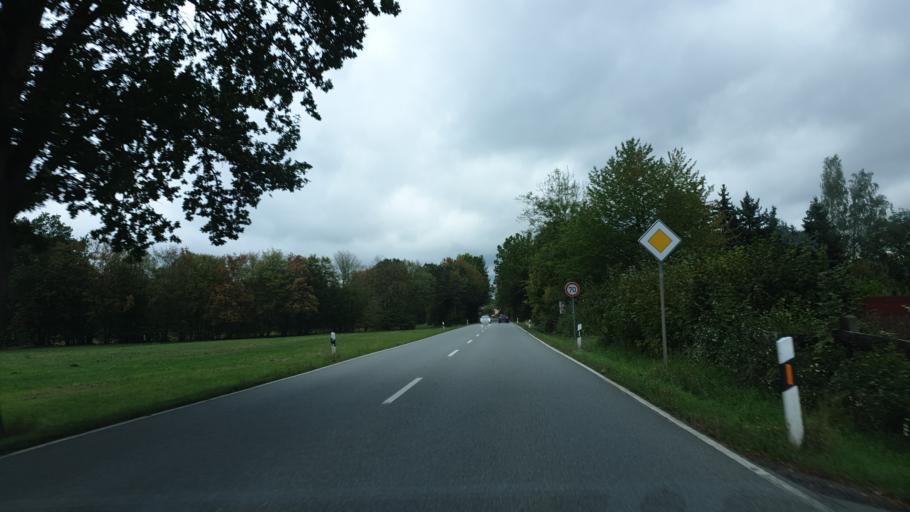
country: DE
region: Saxony
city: Glauchau
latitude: 50.8147
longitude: 12.5704
